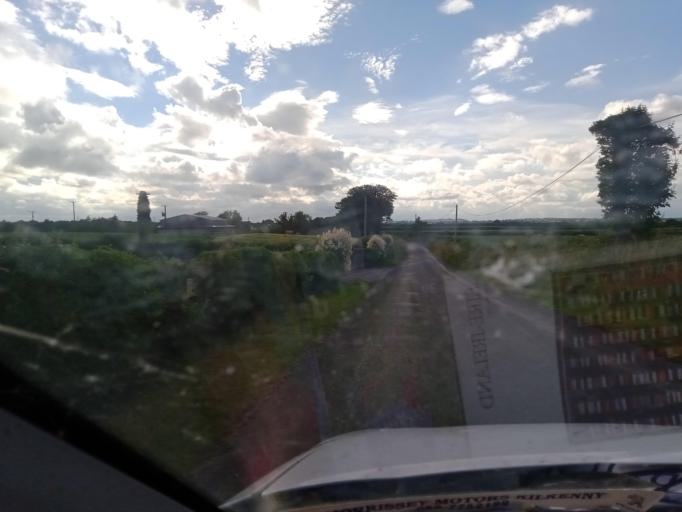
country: IE
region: Leinster
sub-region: Laois
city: Rathdowney
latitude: 52.7740
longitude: -7.5175
